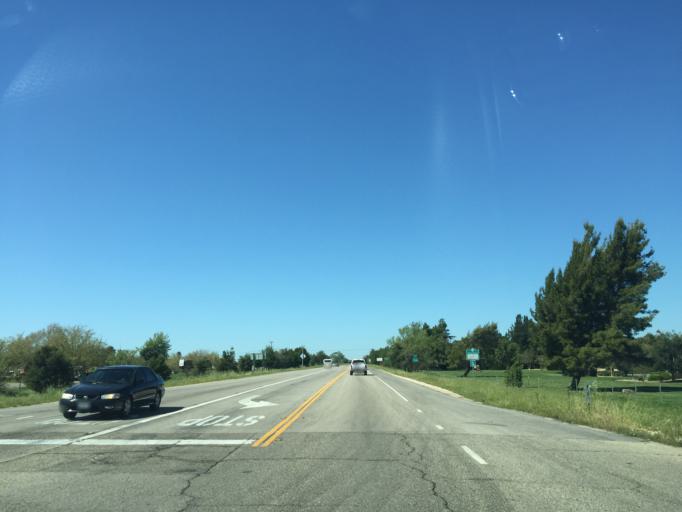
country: US
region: California
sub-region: Santa Barbara County
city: Santa Ynez
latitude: 34.6338
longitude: -120.0811
